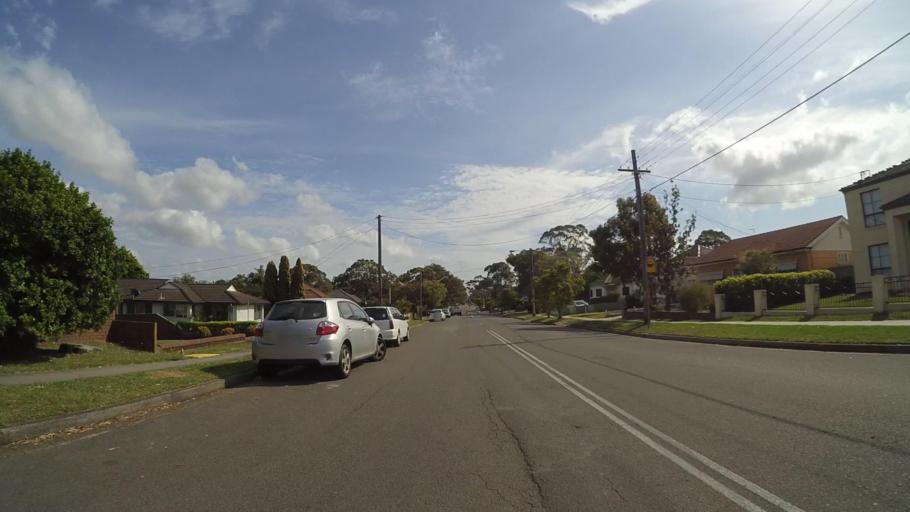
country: AU
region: New South Wales
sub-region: Sutherland Shire
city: Caringbah
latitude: -34.0502
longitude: 151.1162
